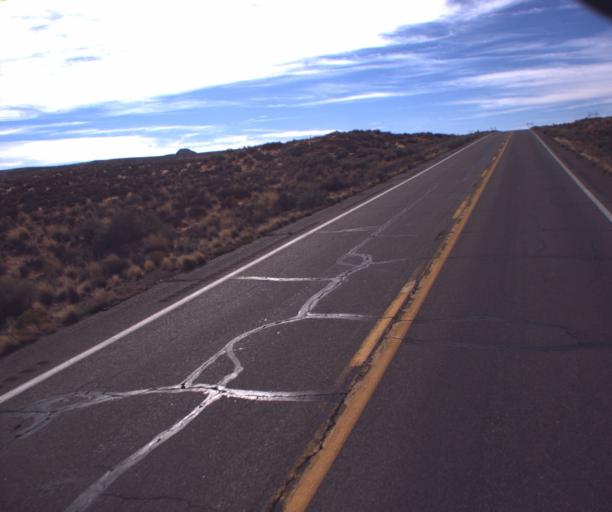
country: US
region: Arizona
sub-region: Coconino County
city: LeChee
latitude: 36.8659
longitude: -111.3401
